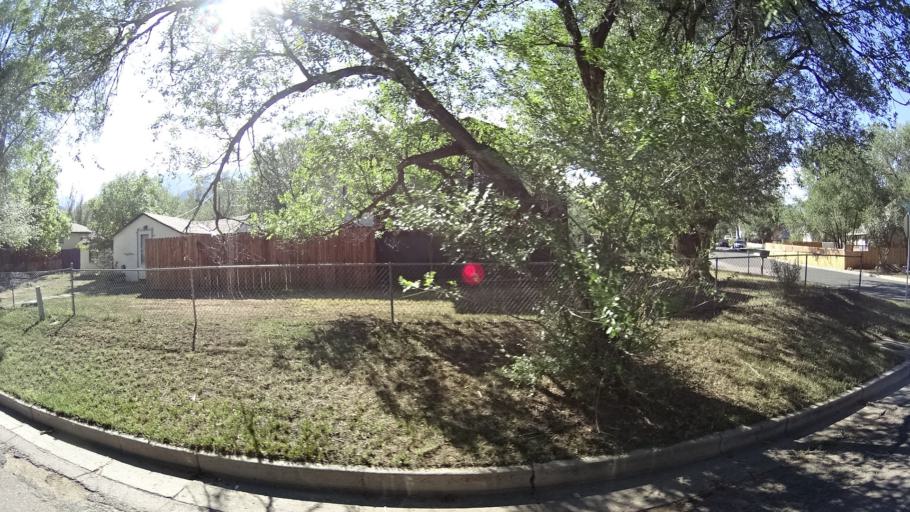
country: US
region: Colorado
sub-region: El Paso County
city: Colorado Springs
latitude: 38.8391
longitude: -104.8670
